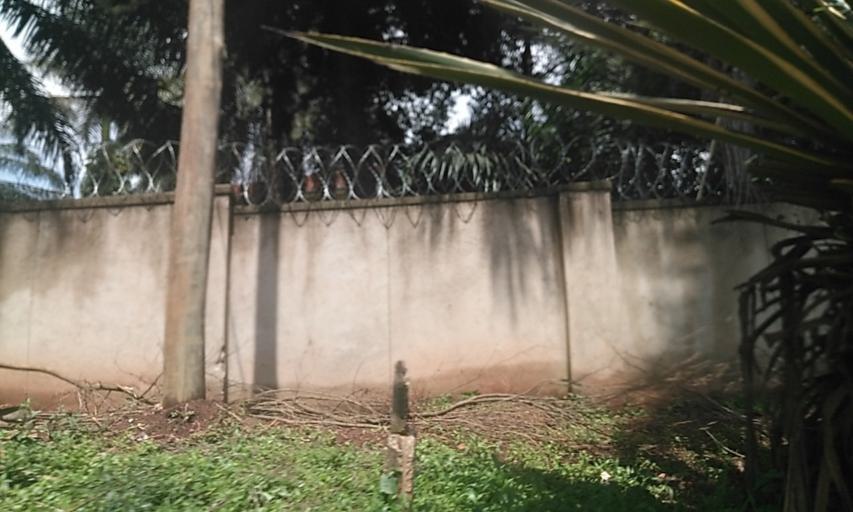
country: UG
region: Central Region
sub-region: Kampala District
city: Kampala
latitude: 0.3346
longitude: 32.6006
